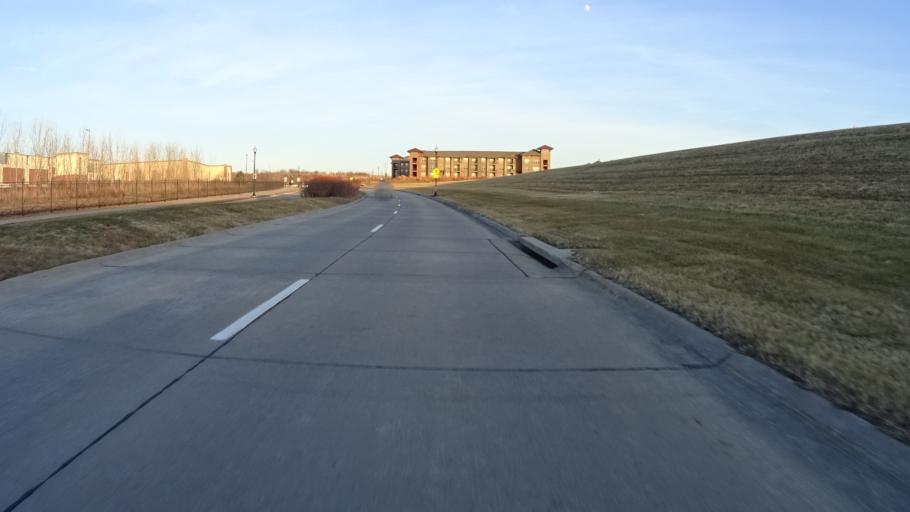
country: US
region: Nebraska
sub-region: Sarpy County
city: Papillion
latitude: 41.1318
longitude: -96.0293
